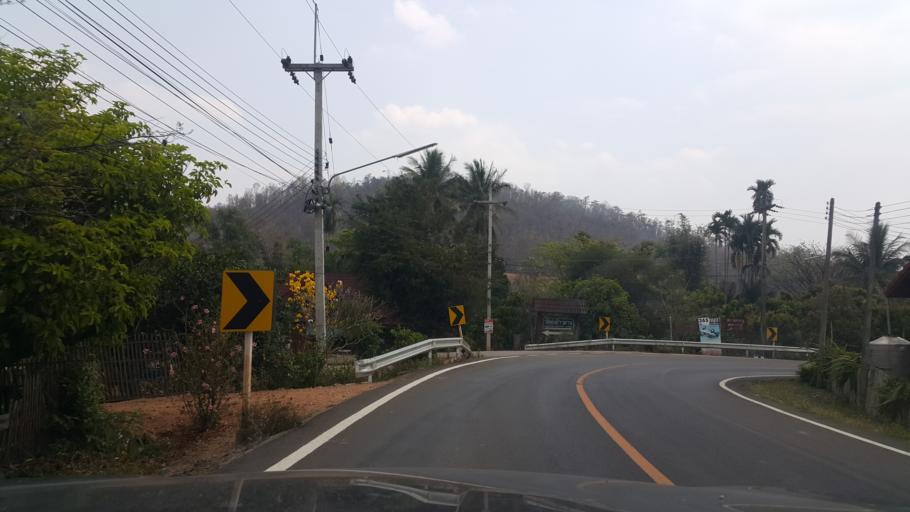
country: TH
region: Lamphun
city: Thung Hua Chang
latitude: 18.1356
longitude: 99.0136
